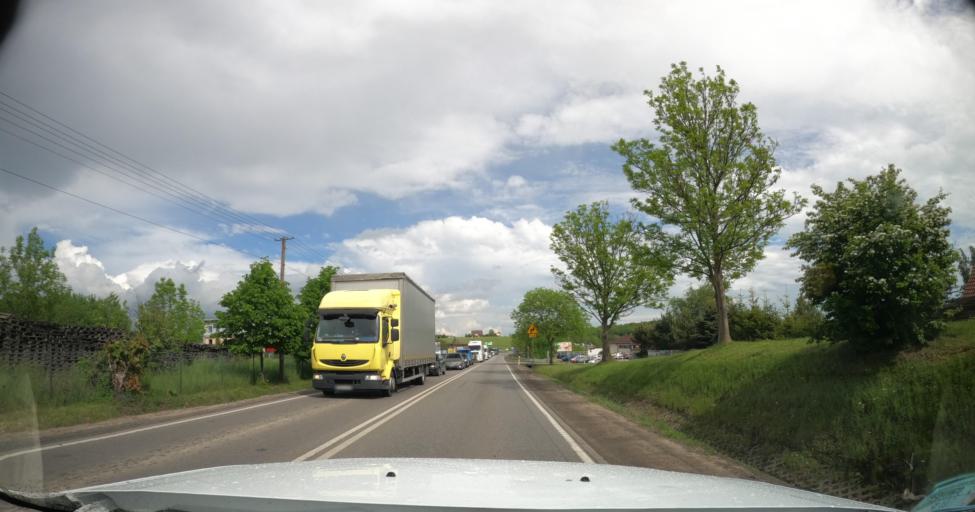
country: PL
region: Pomeranian Voivodeship
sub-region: Powiat kartuski
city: Zukowo
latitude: 54.3411
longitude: 18.3722
